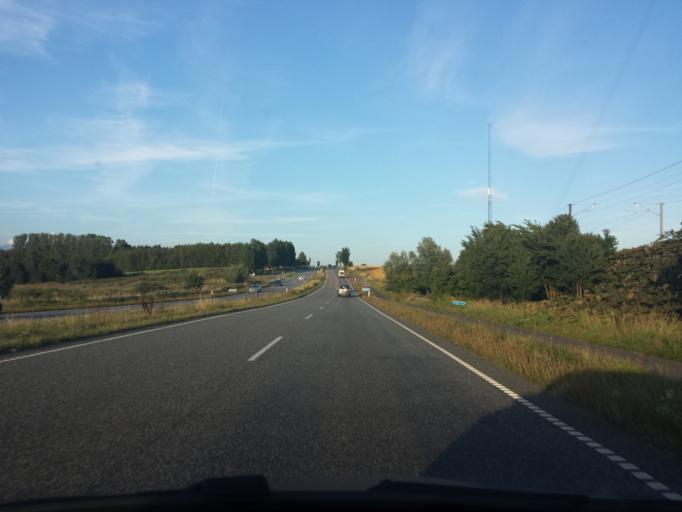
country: DK
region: Capital Region
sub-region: Egedal Kommune
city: Vekso
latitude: 55.7527
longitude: 12.2679
